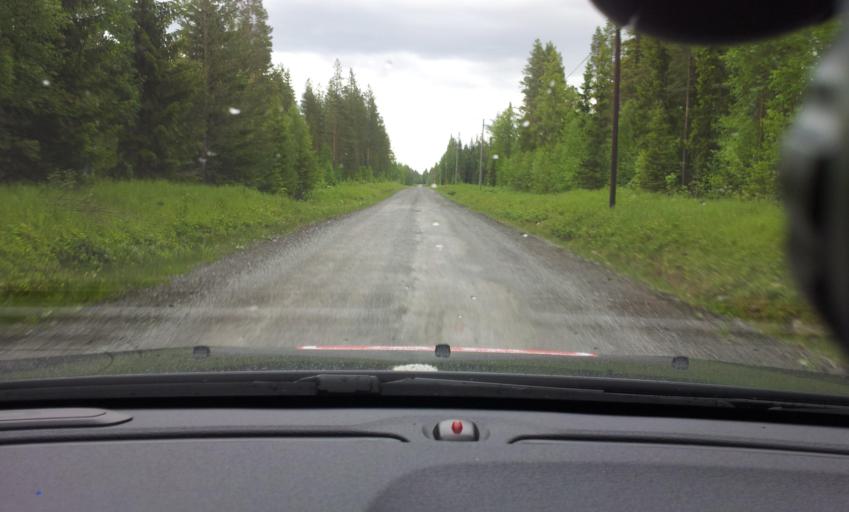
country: SE
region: Jaemtland
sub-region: OEstersunds Kommun
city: Brunflo
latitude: 63.1709
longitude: 14.9752
